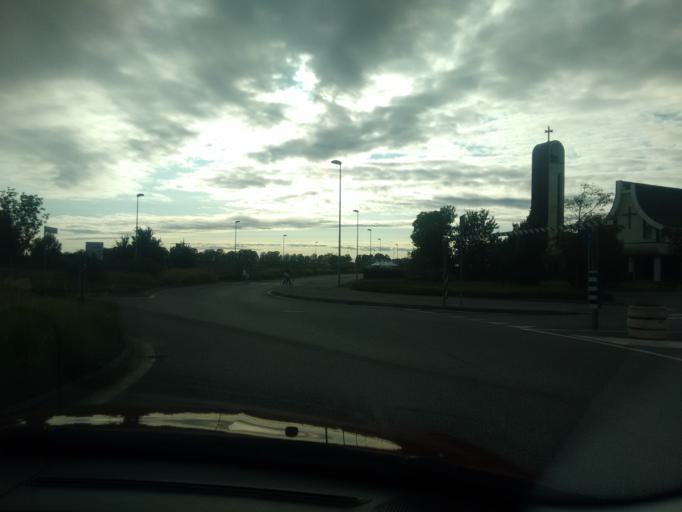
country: IT
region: Veneto
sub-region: Provincia di Venezia
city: Caorle
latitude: 45.5839
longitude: 12.8451
